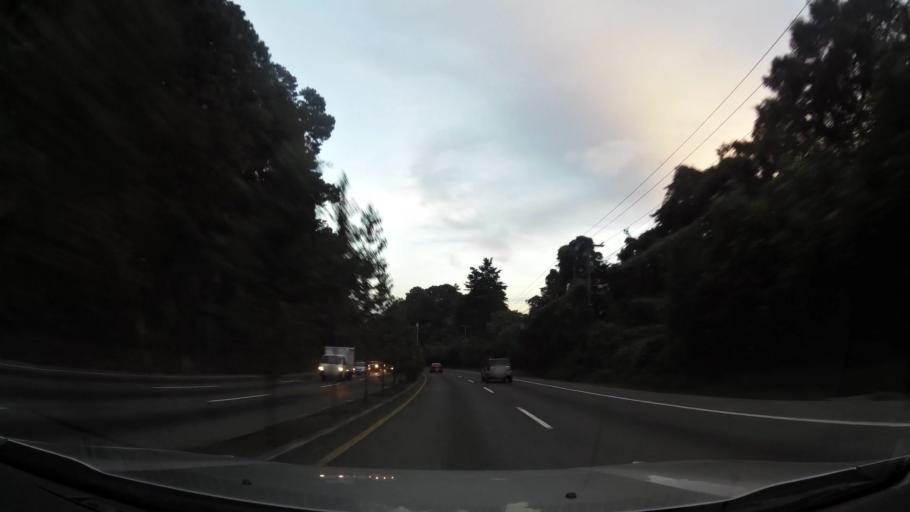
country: GT
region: Sacatepequez
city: San Lucas Sacatepequez
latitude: 14.6078
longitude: -90.6313
